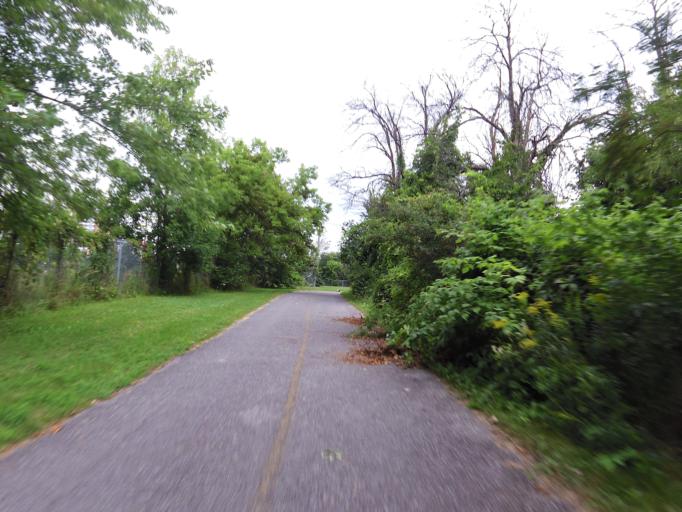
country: CA
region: Ontario
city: Bells Corners
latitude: 45.3427
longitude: -75.8115
